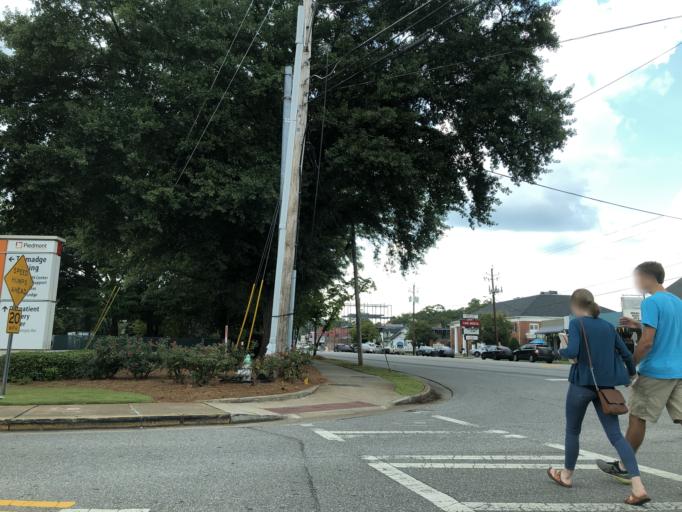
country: US
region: Georgia
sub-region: Clarke County
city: Athens
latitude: 33.9623
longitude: -83.3985
